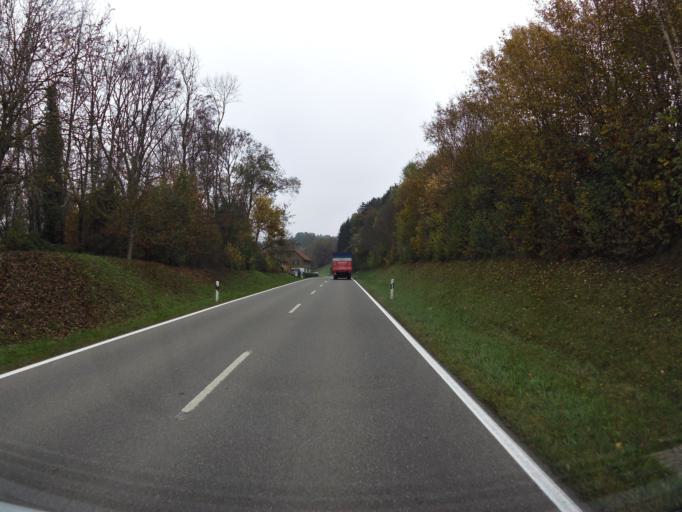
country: DE
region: Baden-Wuerttemberg
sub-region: Freiburg Region
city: Ohningen
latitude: 47.6825
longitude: 8.8955
